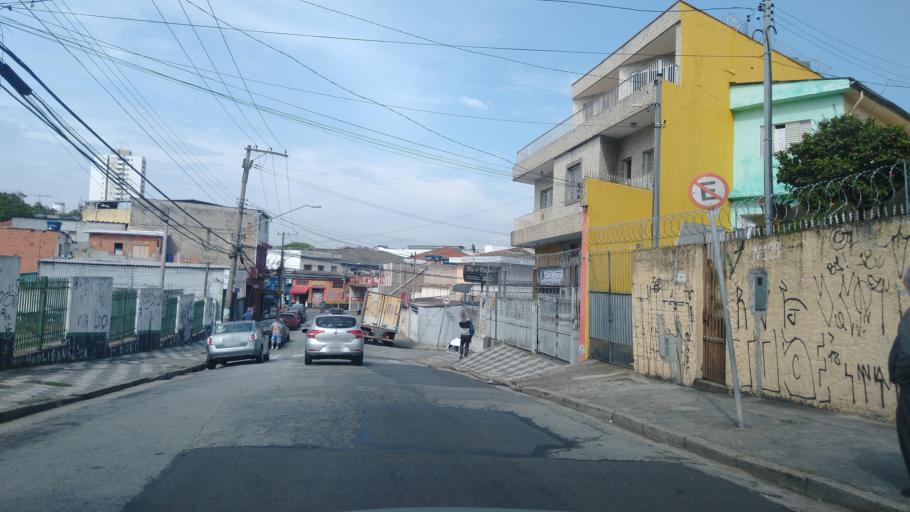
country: BR
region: Sao Paulo
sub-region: Sao Paulo
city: Sao Paulo
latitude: -23.4733
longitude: -46.6681
